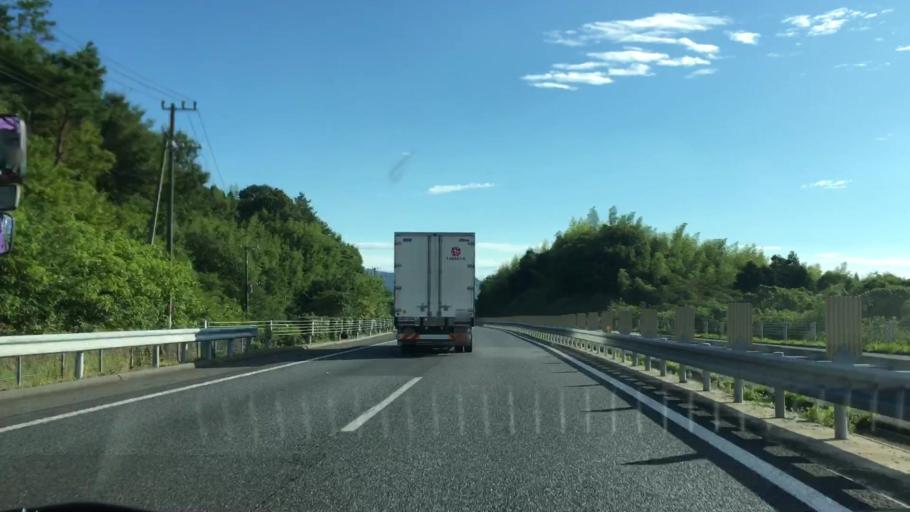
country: JP
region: Yamaguchi
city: Yanai
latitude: 34.0966
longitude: 132.0985
